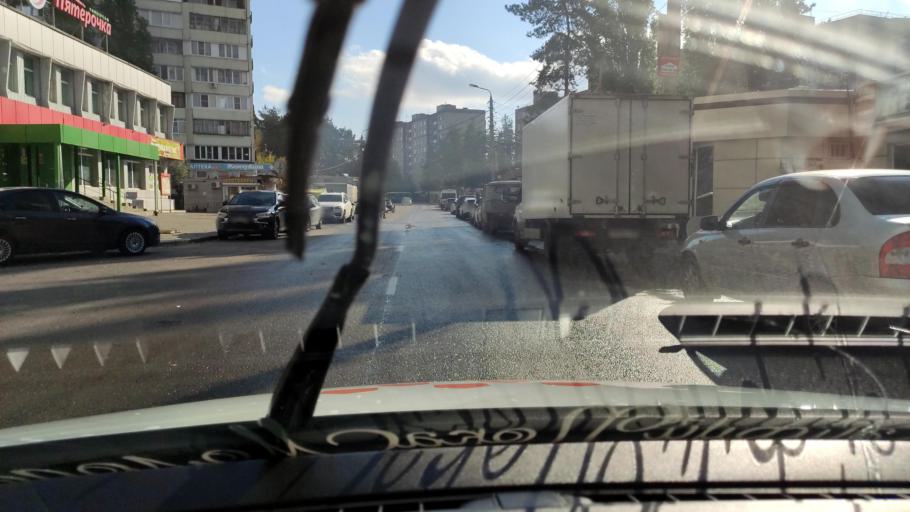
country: RU
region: Voronezj
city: Pridonskoy
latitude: 51.6834
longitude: 39.0838
